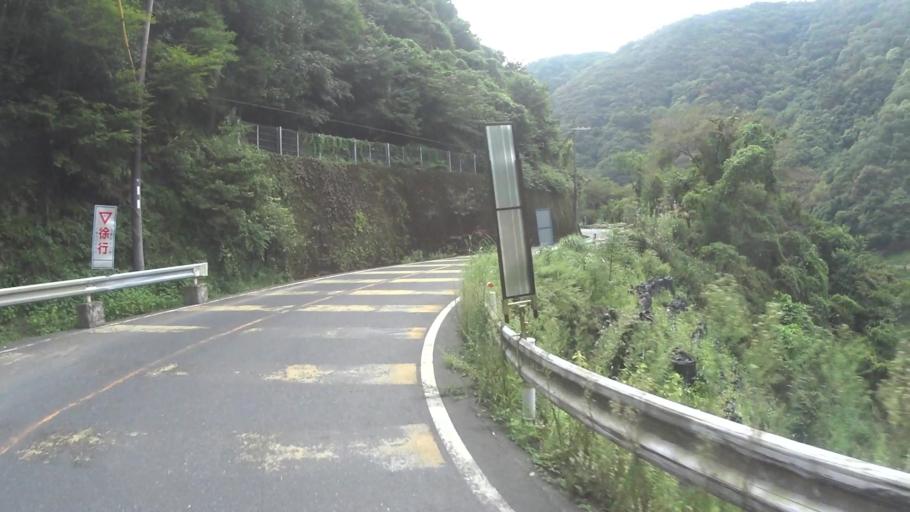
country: JP
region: Kyoto
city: Uji
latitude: 34.8815
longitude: 135.8508
